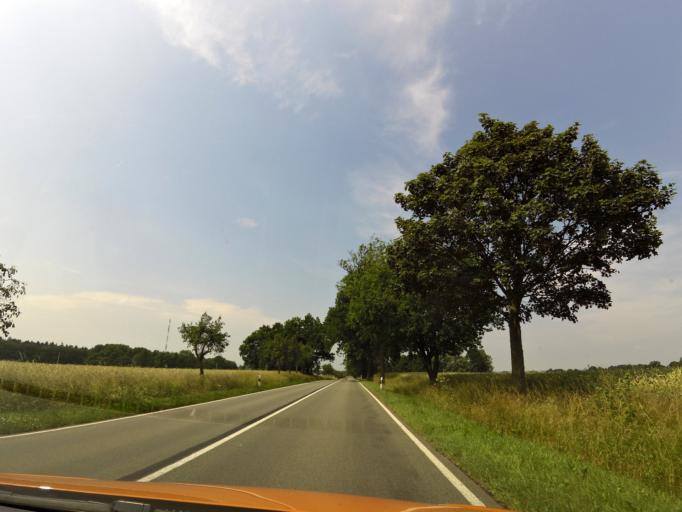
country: DE
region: Brandenburg
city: Pritzwalk
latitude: 53.1015
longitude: 12.1983
